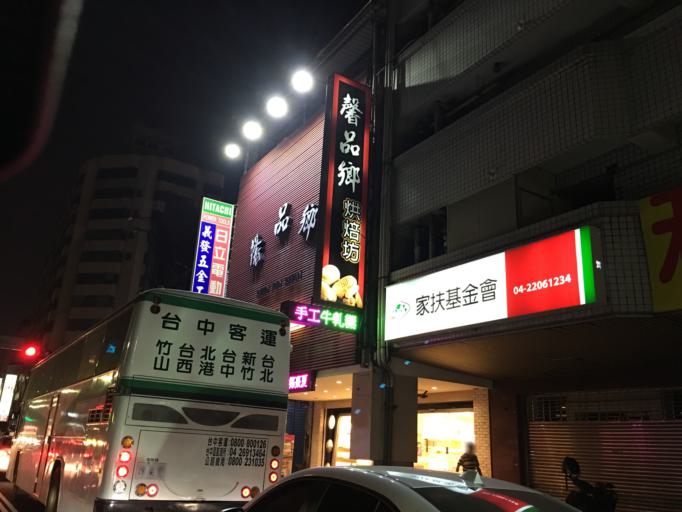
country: TW
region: Taiwan
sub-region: Taichung City
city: Taichung
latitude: 24.1452
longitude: 120.6717
